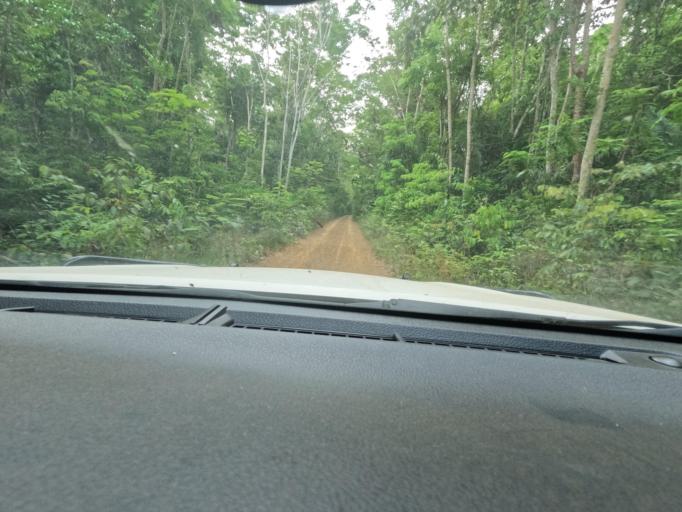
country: BR
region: Rondonia
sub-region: Porto Velho
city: Porto Velho
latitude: -8.6594
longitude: -63.1559
